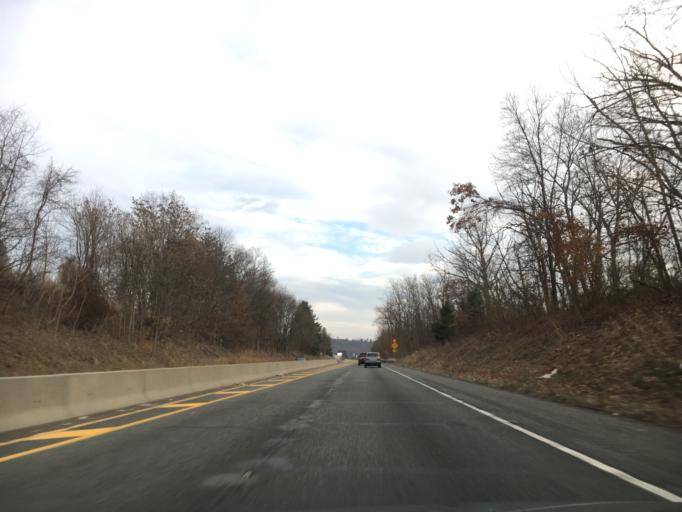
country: US
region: Pennsylvania
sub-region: Carbon County
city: Weissport East
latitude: 40.8238
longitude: -75.6926
